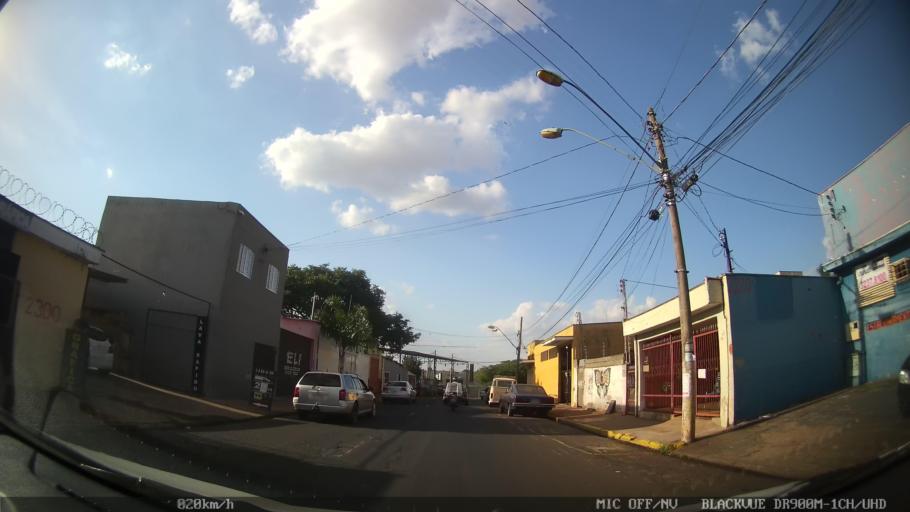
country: BR
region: Sao Paulo
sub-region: Ribeirao Preto
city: Ribeirao Preto
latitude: -21.1491
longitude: -47.8030
